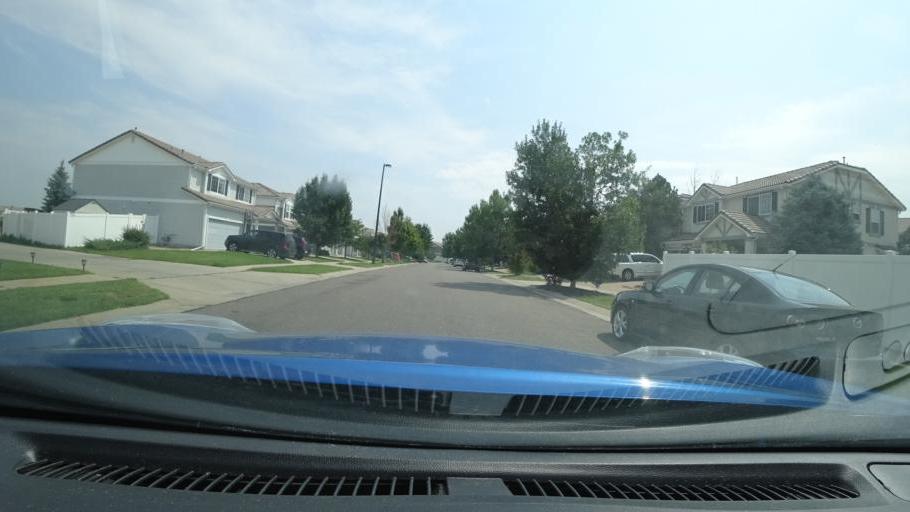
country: US
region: Colorado
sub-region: Adams County
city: Aurora
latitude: 39.7829
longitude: -104.7608
